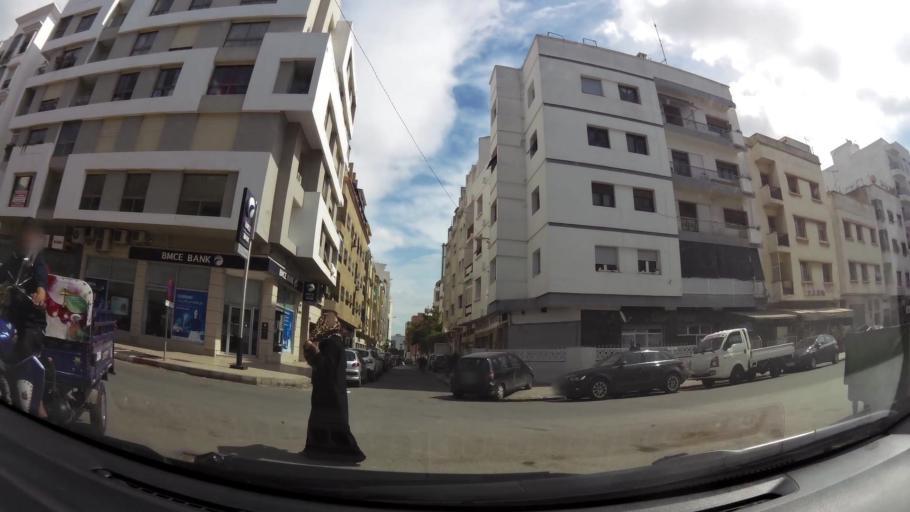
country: MA
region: Grand Casablanca
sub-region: Casablanca
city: Casablanca
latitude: 33.5783
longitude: -7.6386
